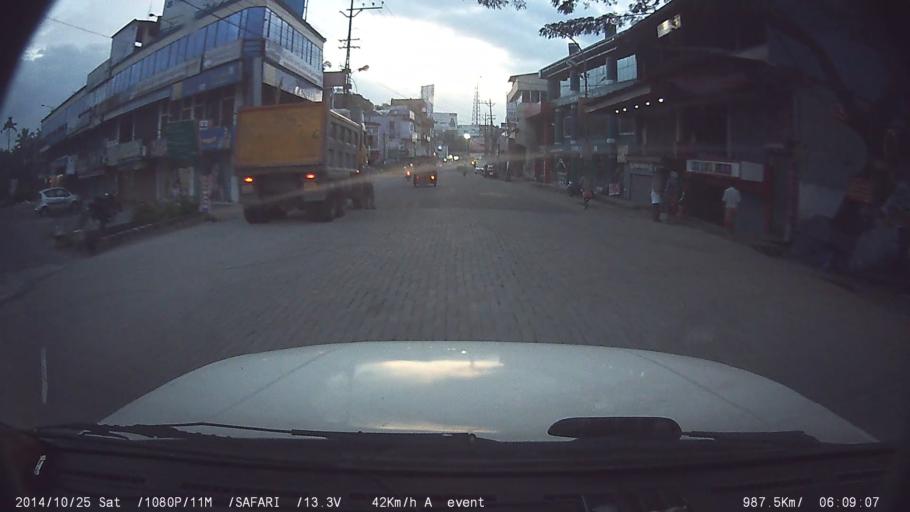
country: IN
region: Kerala
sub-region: Ernakulam
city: Angamali
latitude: 10.1669
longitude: 76.4375
